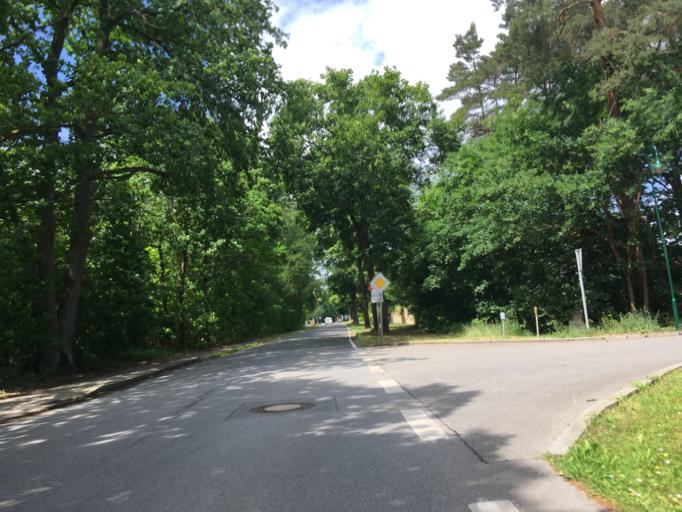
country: DE
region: Brandenburg
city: Wandlitz
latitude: 52.7691
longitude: 13.4565
